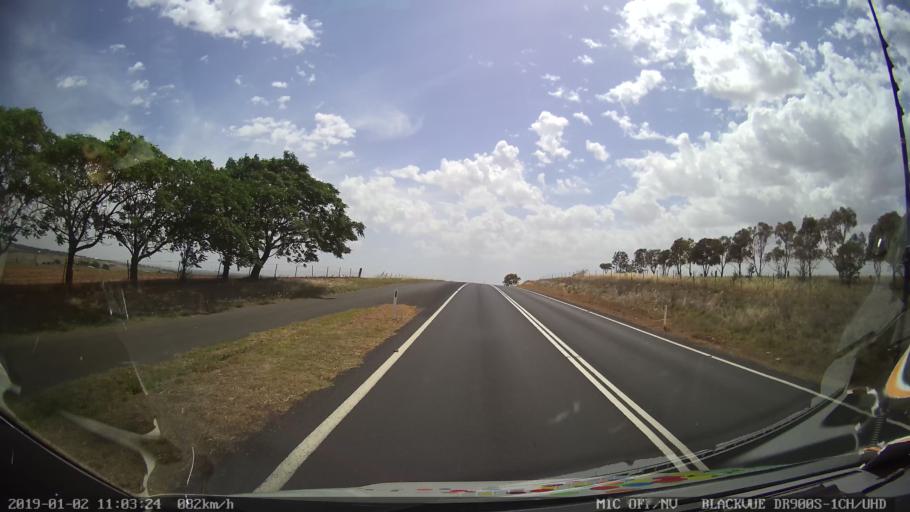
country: AU
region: New South Wales
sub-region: Young
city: Young
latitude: -34.5781
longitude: 148.3377
